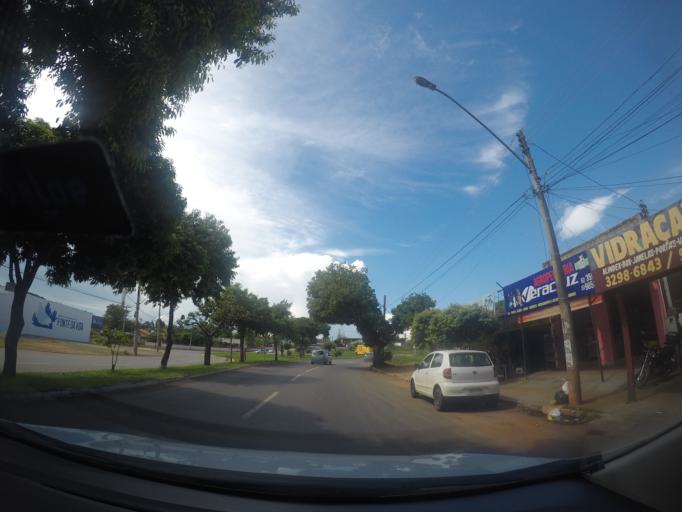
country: BR
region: Goias
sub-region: Trindade
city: Trindade
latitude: -16.6589
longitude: -49.3856
